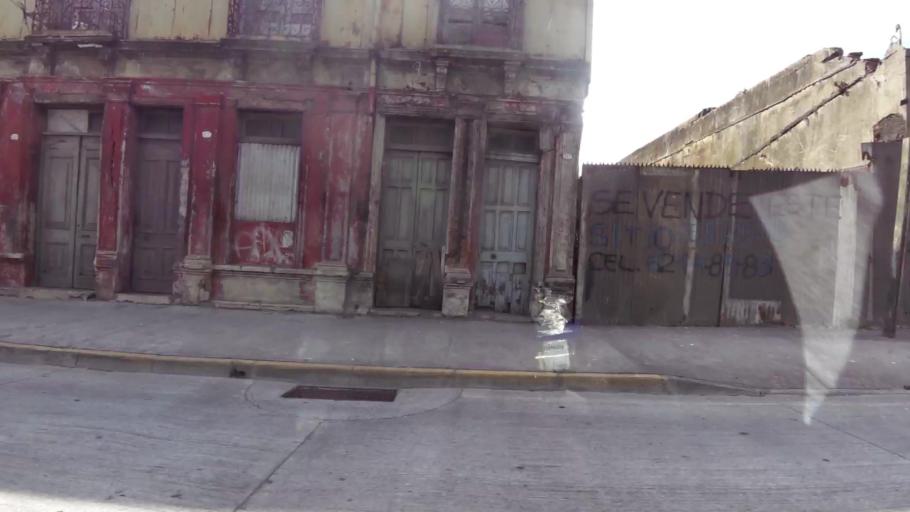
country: CL
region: Biobio
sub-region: Provincia de Concepcion
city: Talcahuano
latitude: -36.7171
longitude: -73.1096
